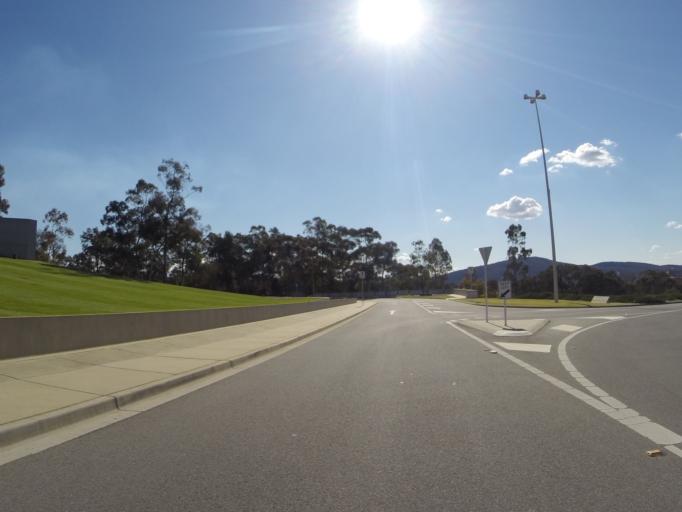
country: AU
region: Australian Capital Territory
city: Forrest
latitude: -35.3060
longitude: 149.1250
